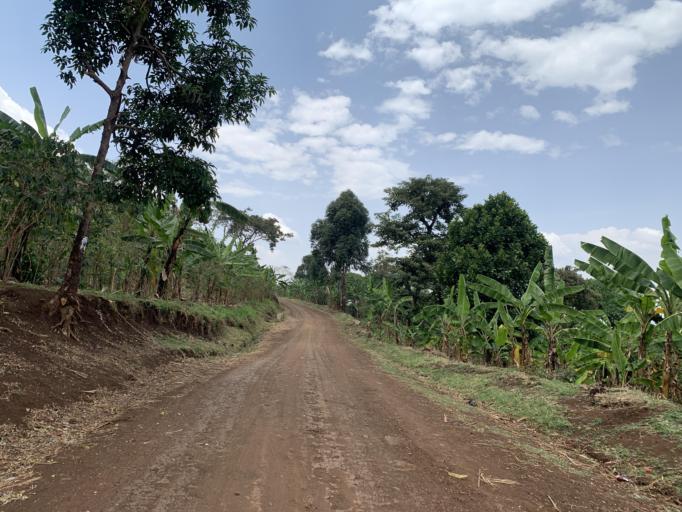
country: UG
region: Eastern Region
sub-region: Sironko District
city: Sironko
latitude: 1.2580
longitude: 34.3092
